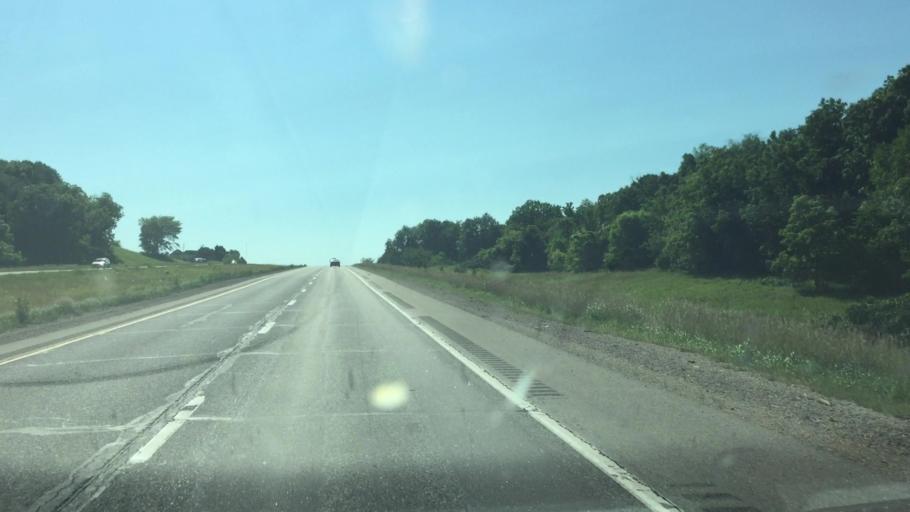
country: US
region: Iowa
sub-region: Linn County
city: Ely
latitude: 41.9257
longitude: -91.5814
